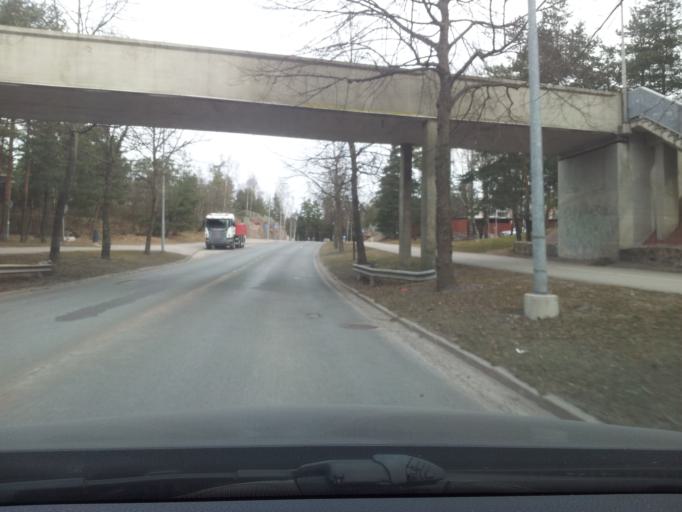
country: FI
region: Uusimaa
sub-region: Helsinki
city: Kauniainen
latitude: 60.1753
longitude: 24.7294
